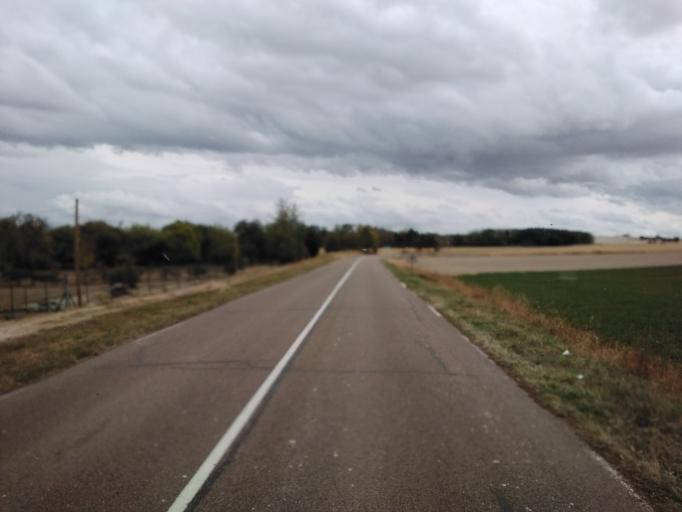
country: FR
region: Champagne-Ardenne
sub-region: Departement de la Marne
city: Frignicourt
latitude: 48.6688
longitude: 4.5840
